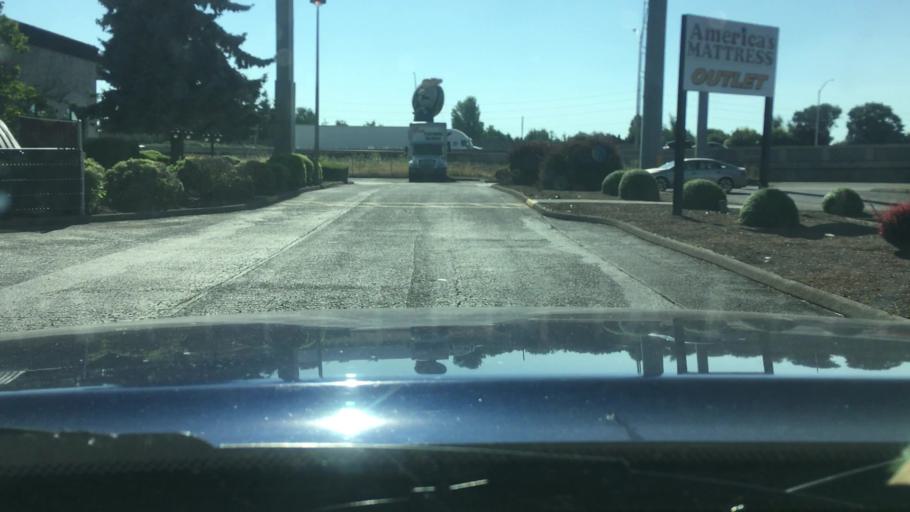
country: US
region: Oregon
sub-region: Lane County
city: Springfield
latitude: 44.0800
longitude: -123.0458
